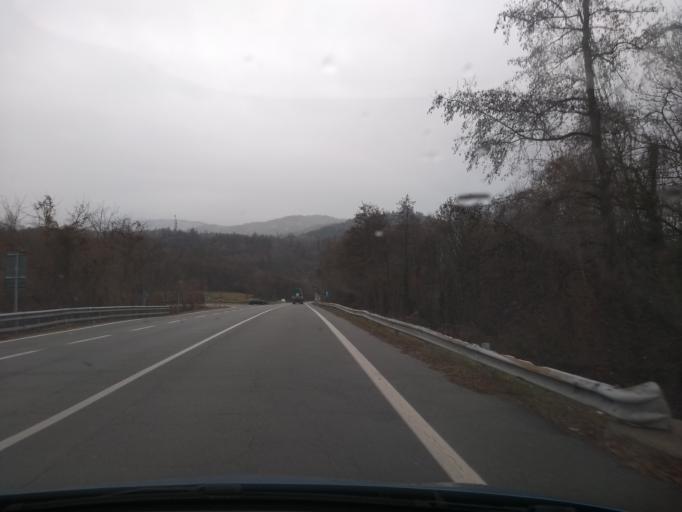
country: IT
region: Piedmont
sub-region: Provincia di Torino
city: Baldissero Canavese
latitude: 45.4087
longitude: 7.7548
